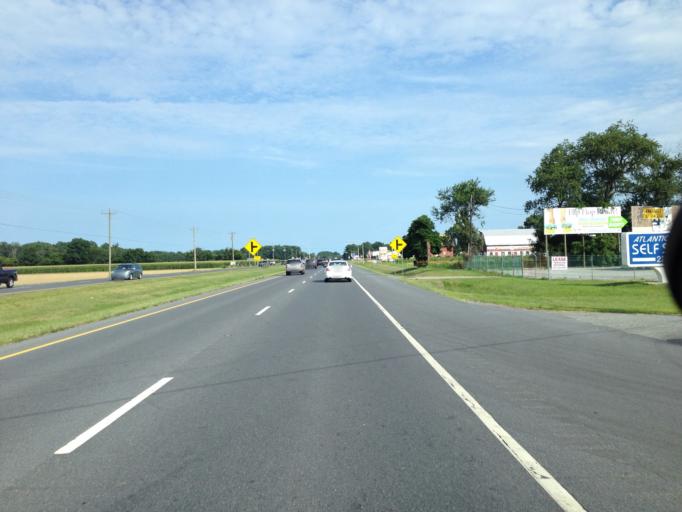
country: US
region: Delaware
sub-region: Sussex County
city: Lewes
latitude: 38.7692
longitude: -75.2171
